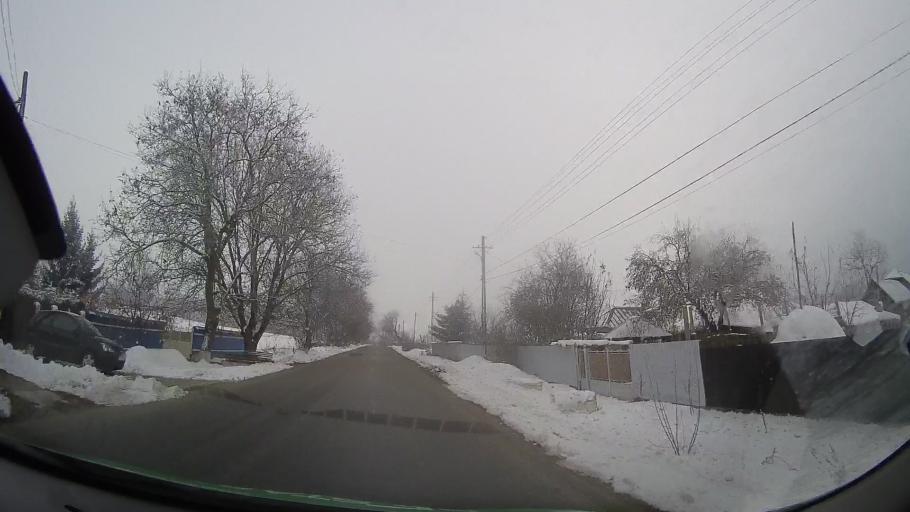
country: RO
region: Bacau
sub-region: Comuna Stanisesti
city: Stanisesti
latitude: 46.4373
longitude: 27.2673
